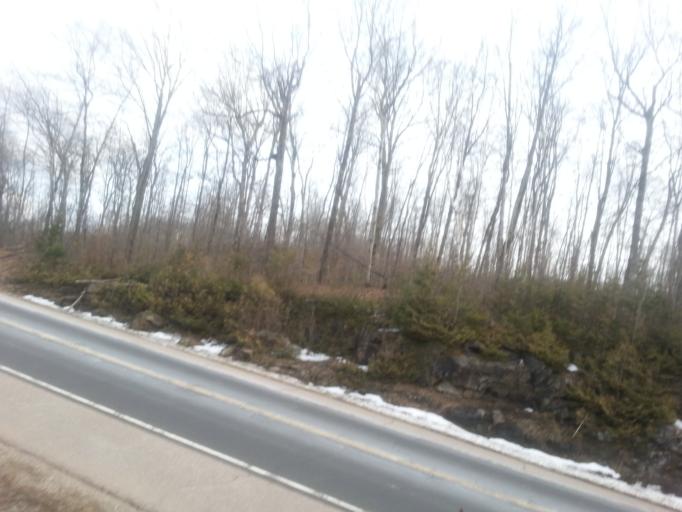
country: CA
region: Ontario
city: Omemee
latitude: 44.8202
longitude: -78.7725
